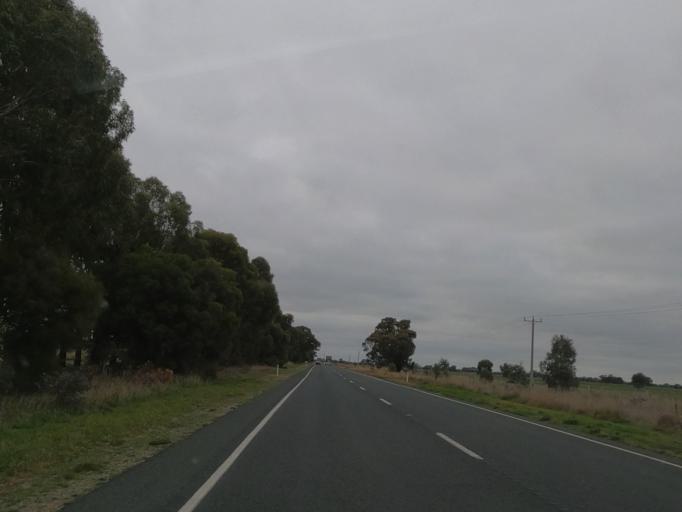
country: AU
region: Victoria
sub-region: Greater Bendigo
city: Long Gully
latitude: -36.3564
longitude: 143.9769
